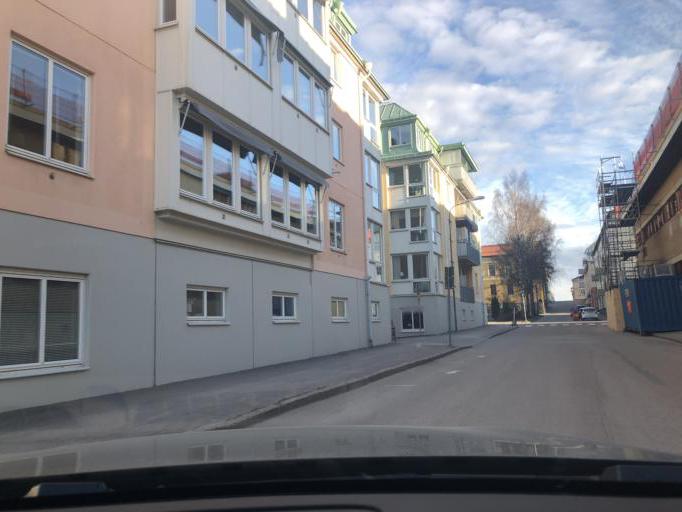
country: SE
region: Gaevleborg
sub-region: Hudiksvalls Kommun
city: Hudiksvall
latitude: 61.7292
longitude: 17.1129
